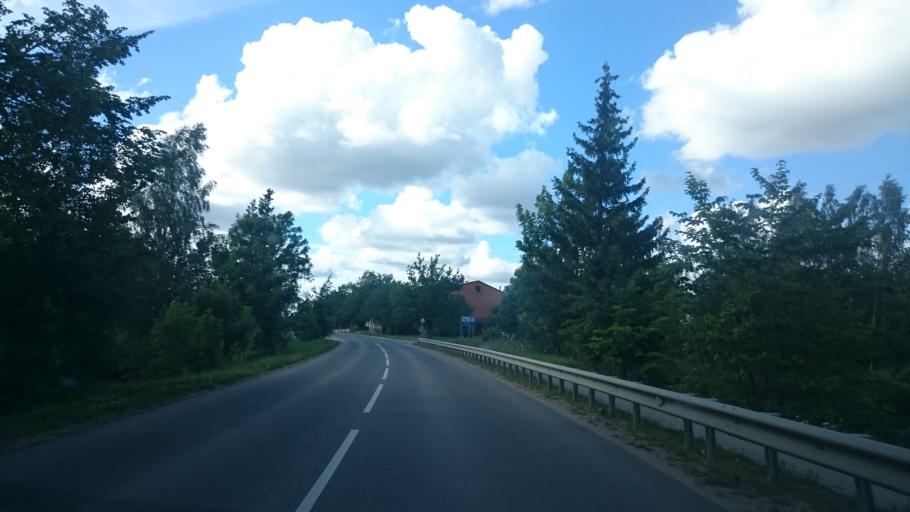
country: LV
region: Aizpute
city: Aizpute
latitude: 56.7054
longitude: 21.6246
